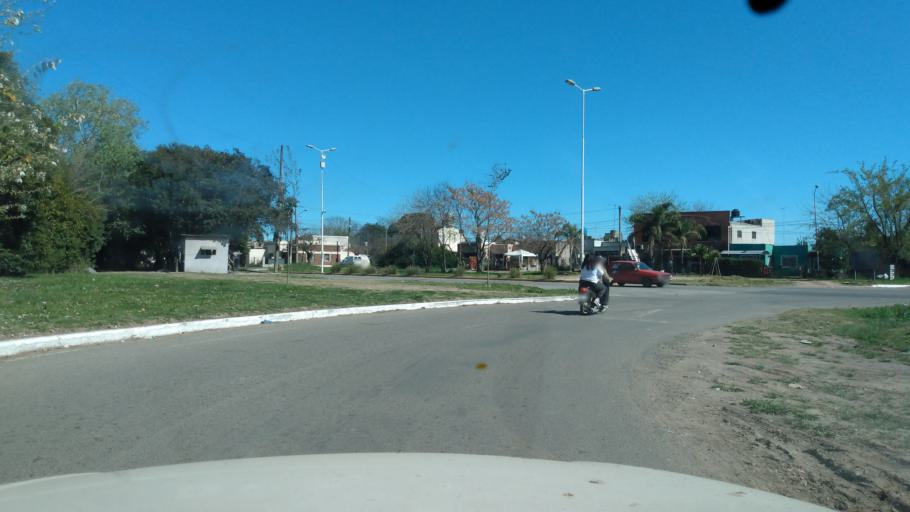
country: AR
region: Buenos Aires
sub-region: Partido de Lujan
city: Lujan
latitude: -34.5571
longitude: -59.1009
